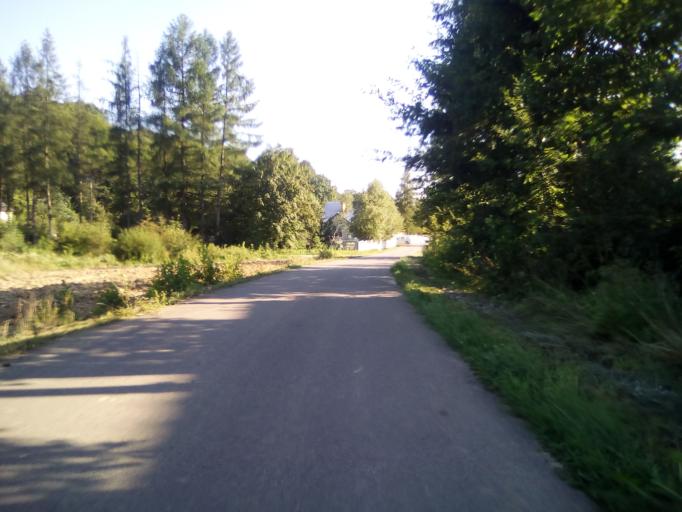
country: PL
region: Subcarpathian Voivodeship
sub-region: Powiat brzozowski
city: Domaradz
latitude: 49.8094
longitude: 21.9445
